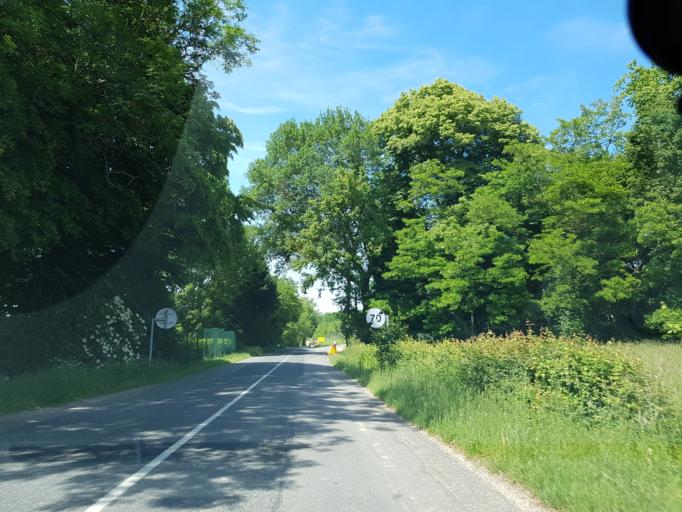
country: FR
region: Rhone-Alpes
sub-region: Departement de l'Ain
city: Montagnat
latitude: 46.1863
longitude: 5.2721
